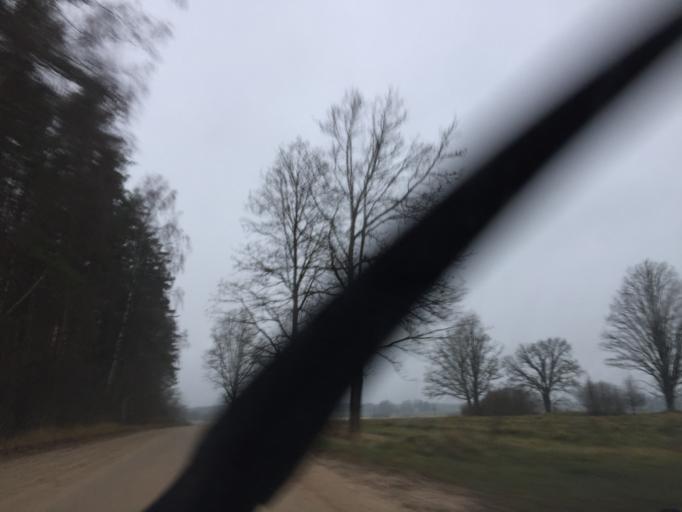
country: LV
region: Koceni
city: Koceni
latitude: 57.5430
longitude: 25.3294
